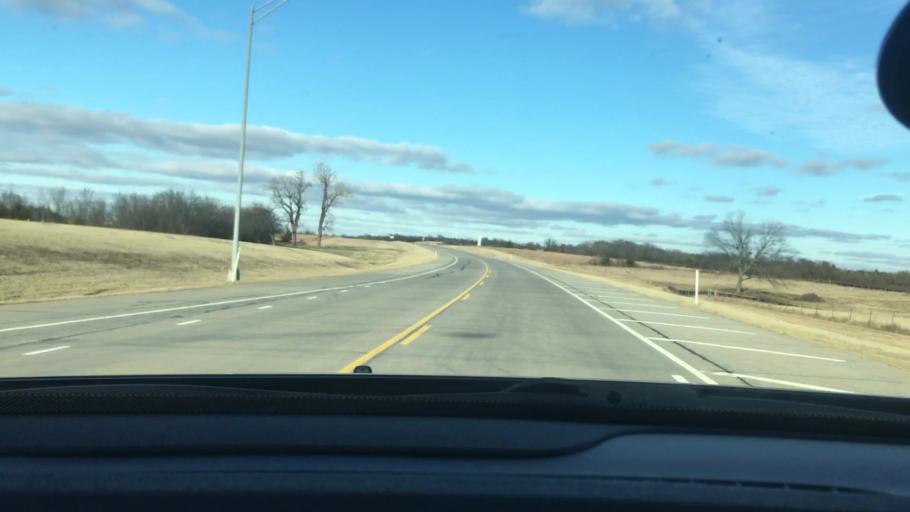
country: US
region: Oklahoma
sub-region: Murray County
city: Sulphur
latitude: 34.5696
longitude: -96.9276
